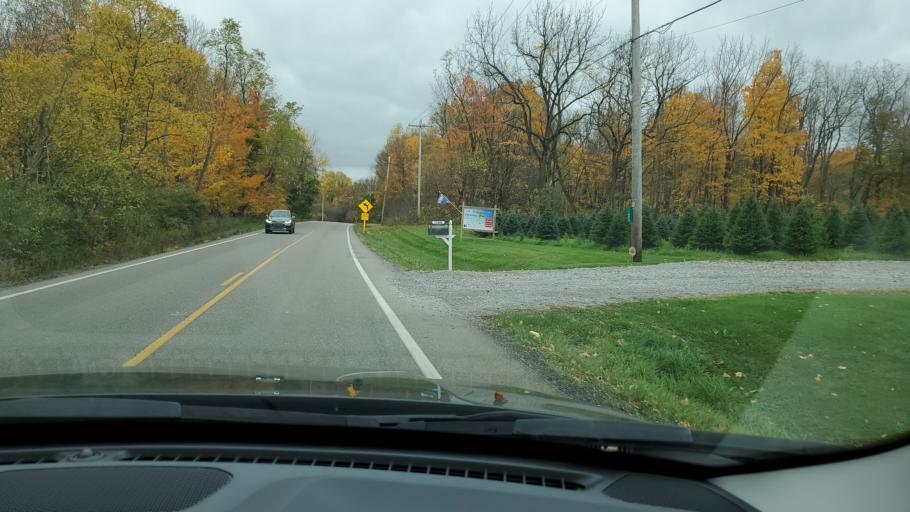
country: US
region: Ohio
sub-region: Mahoning County
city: Boardman
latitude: 40.9527
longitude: -80.6415
